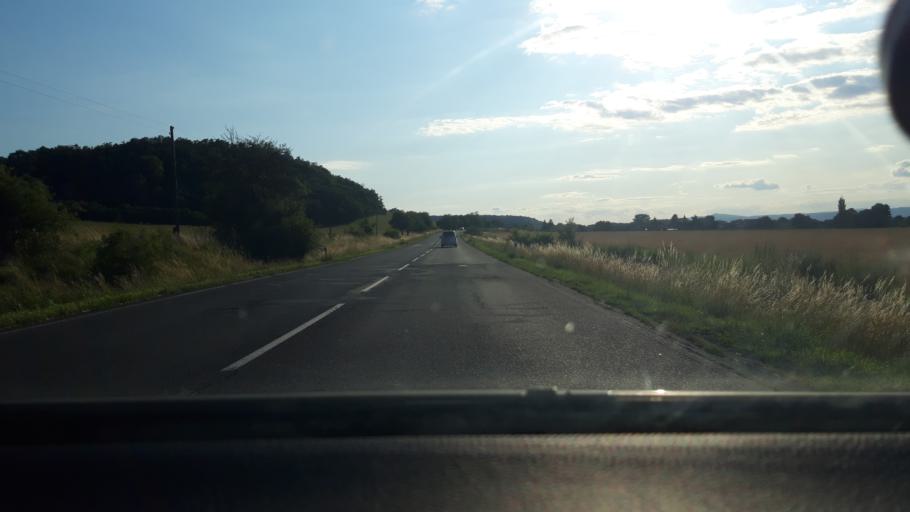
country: SK
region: Banskobystricky
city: Fil'akovo
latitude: 48.2903
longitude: 19.7873
